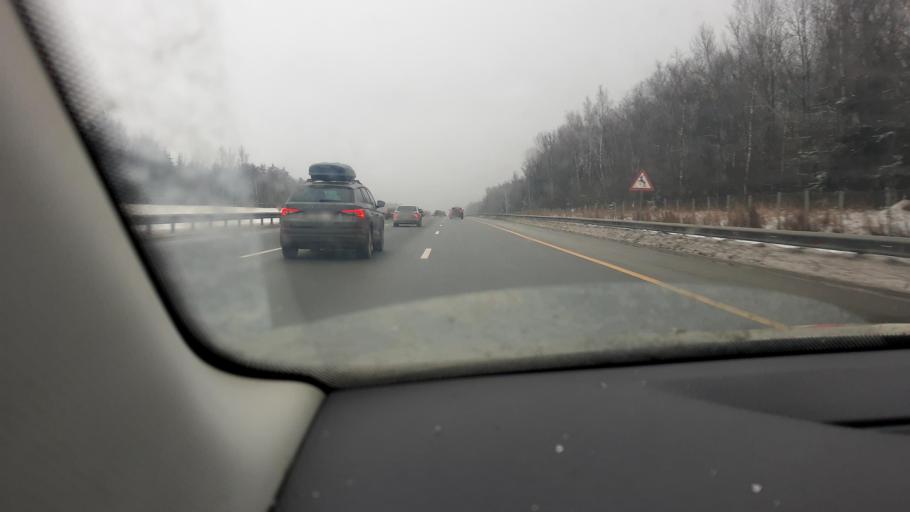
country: RU
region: Moskovskaya
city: Zhilevo
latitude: 54.9567
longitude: 37.9809
